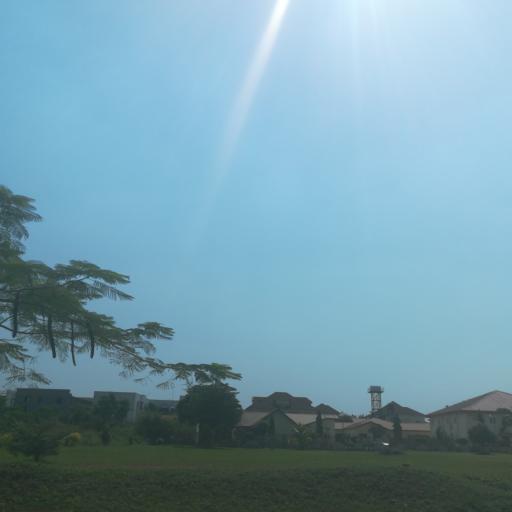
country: NG
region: Abuja Federal Capital Territory
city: Abuja
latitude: 9.0773
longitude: 7.4322
